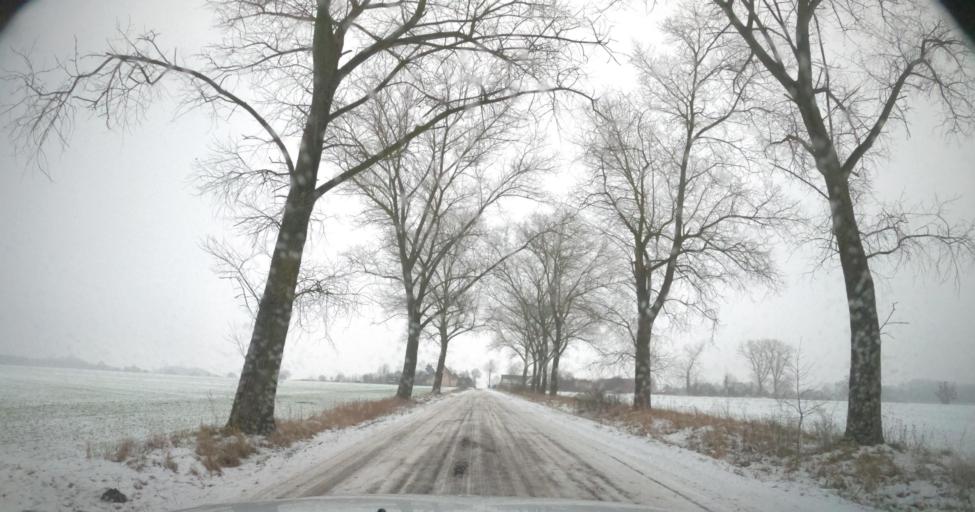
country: PL
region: West Pomeranian Voivodeship
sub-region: Powiat gryficki
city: Brojce
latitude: 53.8991
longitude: 15.3125
